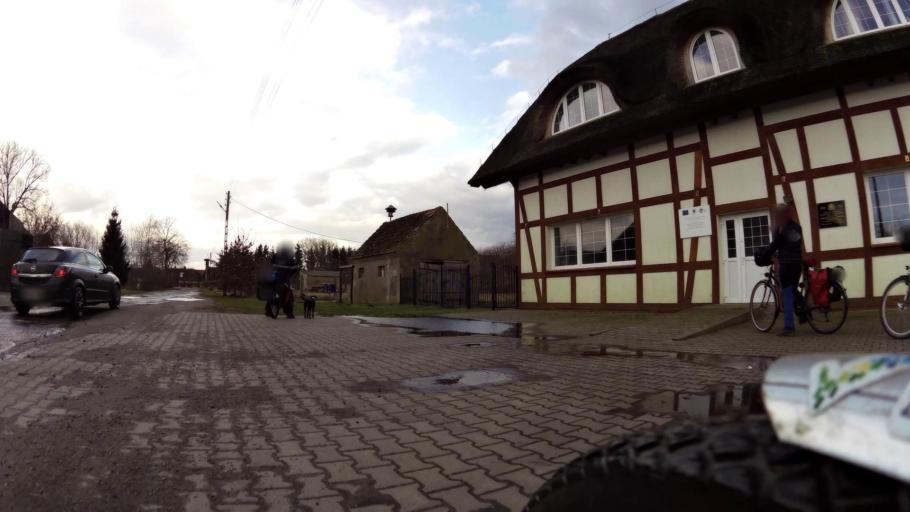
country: PL
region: West Pomeranian Voivodeship
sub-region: Powiat kamienski
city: Kamien Pomorski
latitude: 53.8945
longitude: 14.7266
